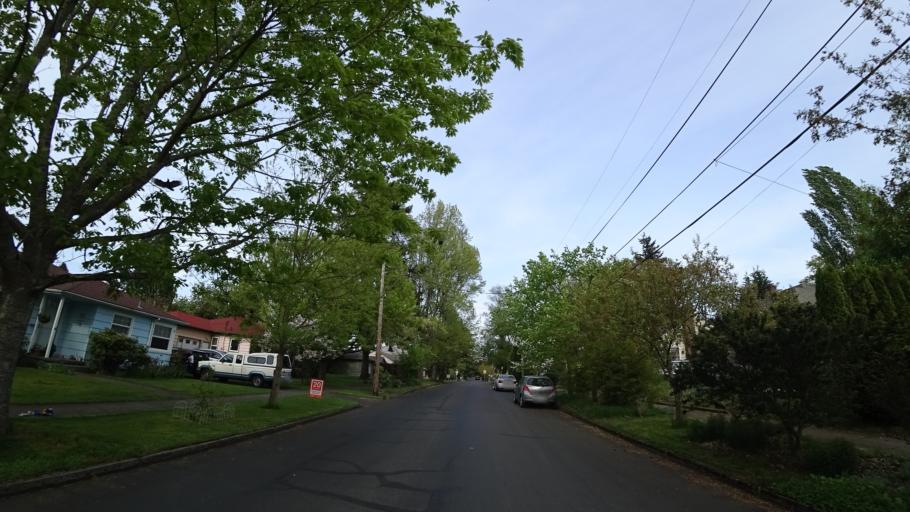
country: US
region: Oregon
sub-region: Clackamas County
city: Milwaukie
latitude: 45.4712
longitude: -122.6173
